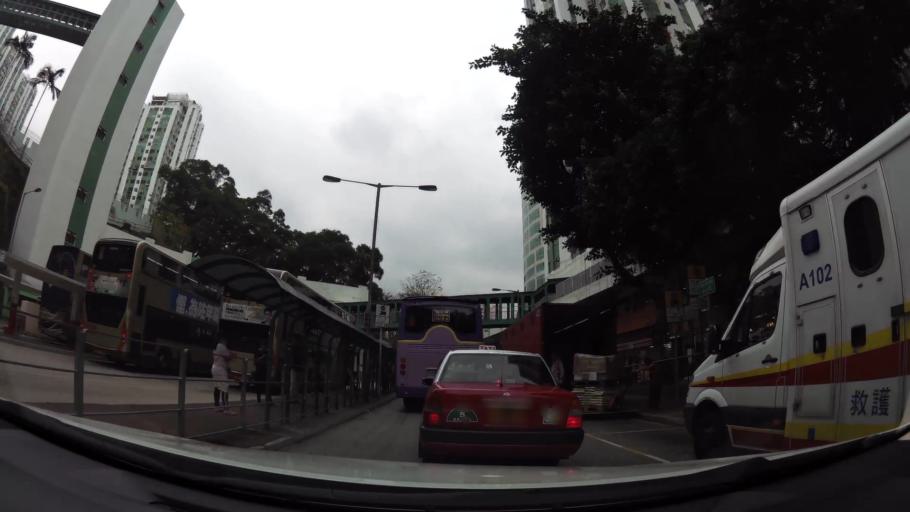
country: HK
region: Tsuen Wan
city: Tsuen Wan
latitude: 22.3773
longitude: 114.1038
